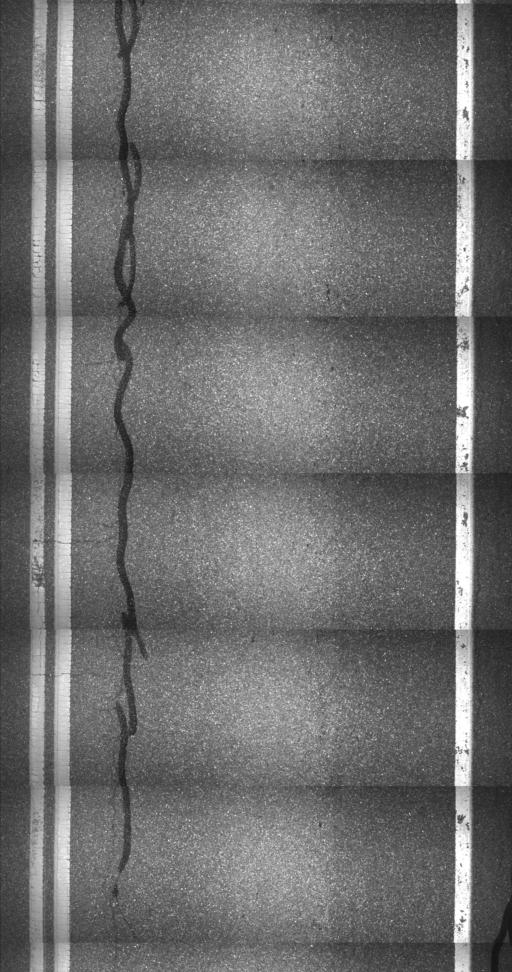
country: US
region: Vermont
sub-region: Franklin County
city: Saint Albans
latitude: 44.7695
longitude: -73.0821
